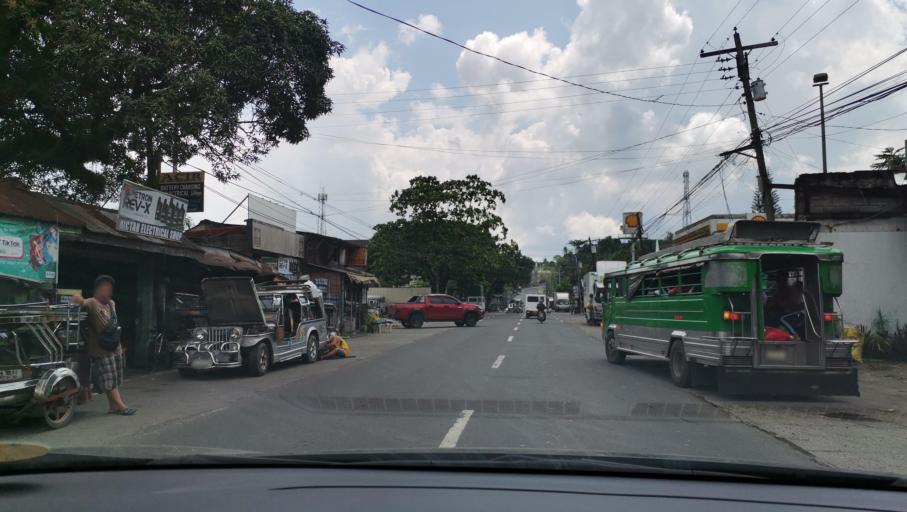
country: PH
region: Calabarzon
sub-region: Province of Quezon
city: Calauag
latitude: 13.9531
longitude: 122.2976
